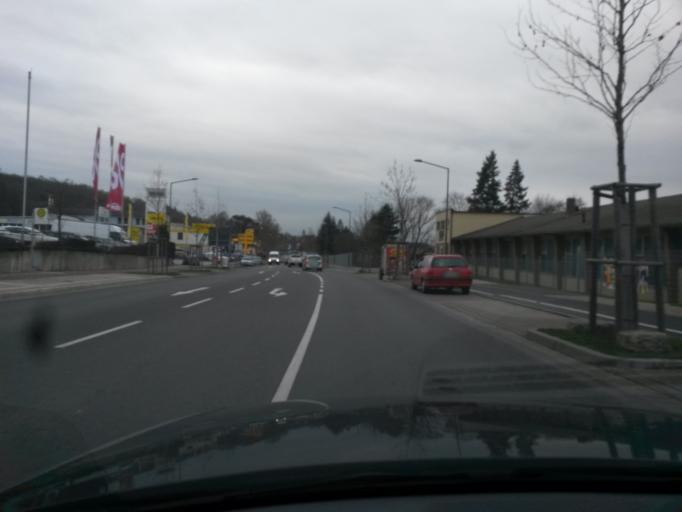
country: DE
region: Bavaria
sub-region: Regierungsbezirk Unterfranken
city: Gerbrunn
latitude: 49.7963
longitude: 9.9777
